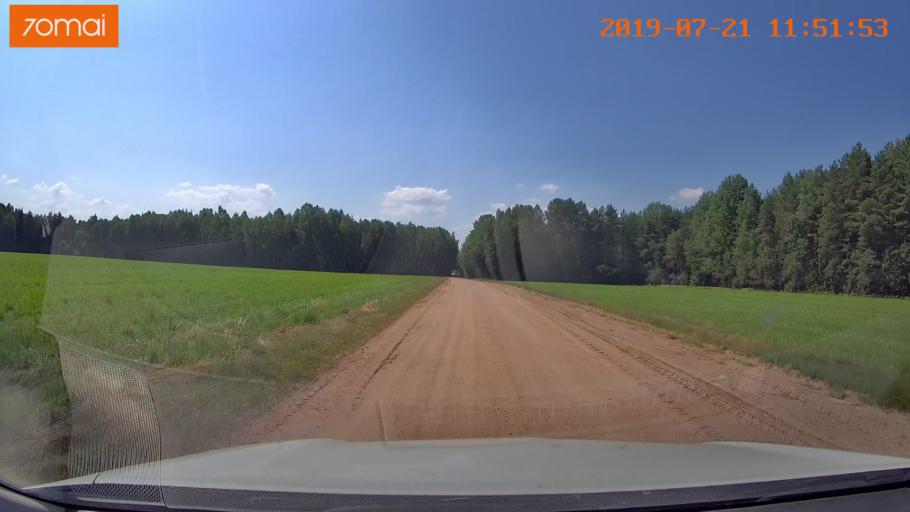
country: BY
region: Grodnenskaya
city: Lyubcha
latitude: 53.8812
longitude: 26.0103
